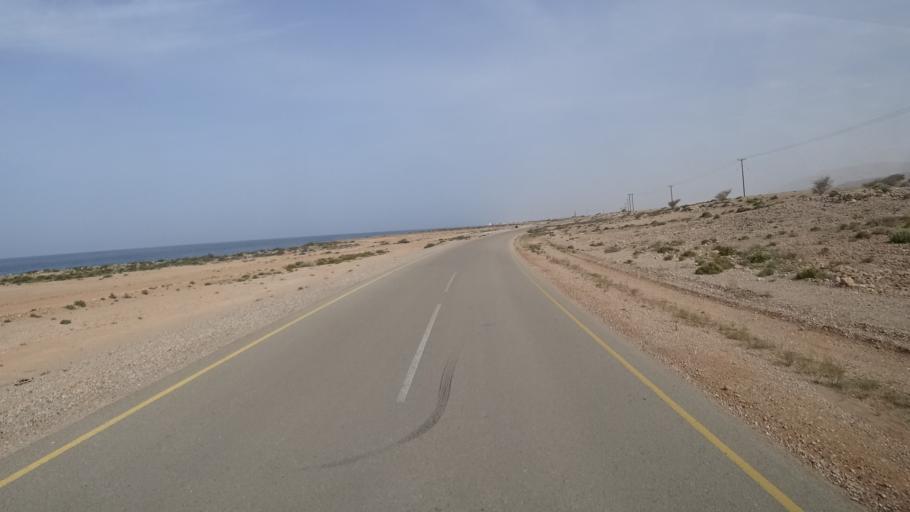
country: OM
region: Ash Sharqiyah
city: Al Qabil
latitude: 23.0091
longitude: 59.1096
